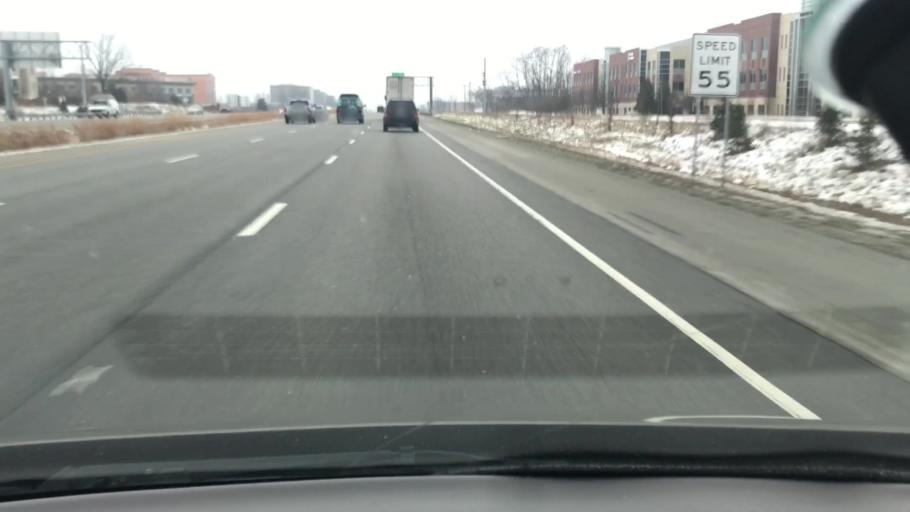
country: US
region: Indiana
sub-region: Hamilton County
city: Carmel
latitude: 39.9689
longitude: -86.1580
